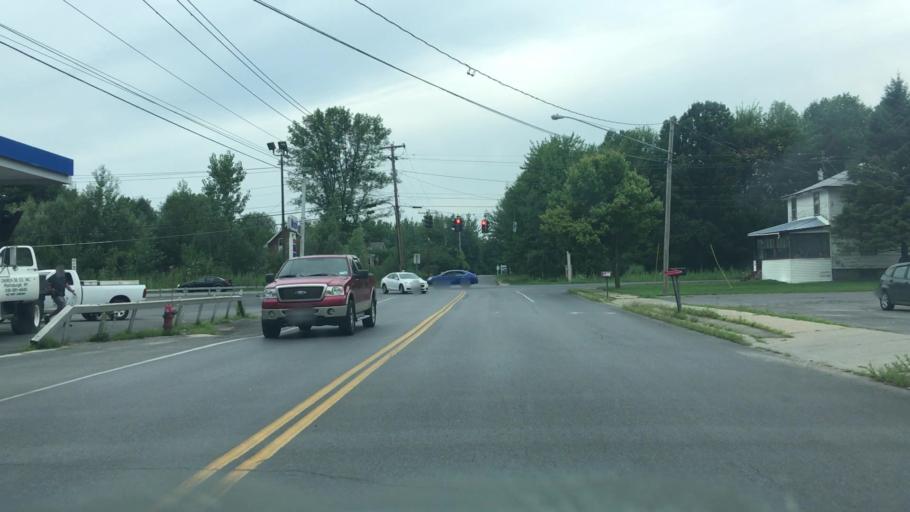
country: US
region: New York
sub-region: Clinton County
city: Plattsburgh West
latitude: 44.6859
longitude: -73.5064
